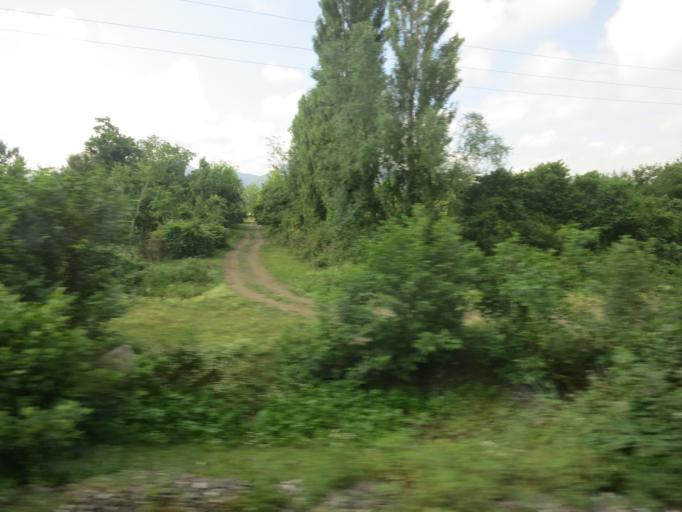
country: GE
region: Guria
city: Lanchkhuti
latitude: 42.0965
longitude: 42.0257
